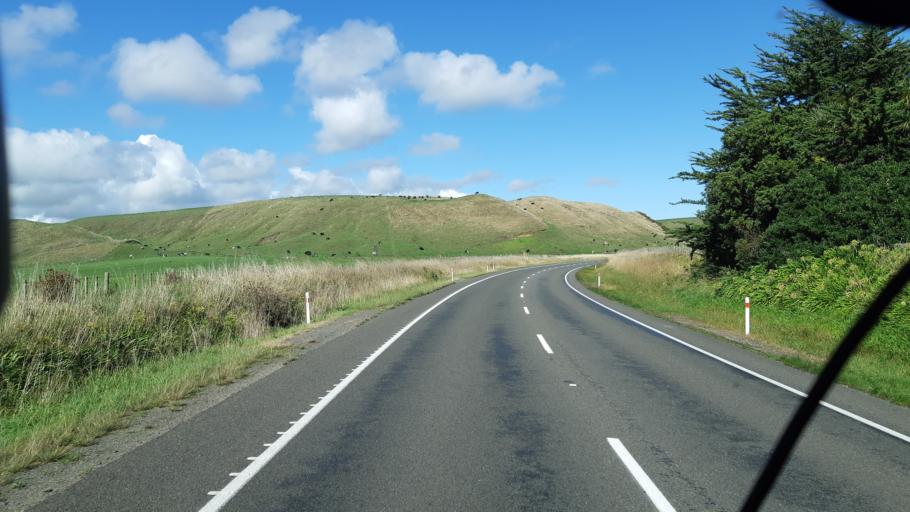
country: NZ
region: Manawatu-Wanganui
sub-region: Wanganui District
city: Wanganui
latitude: -40.0112
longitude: 175.1718
